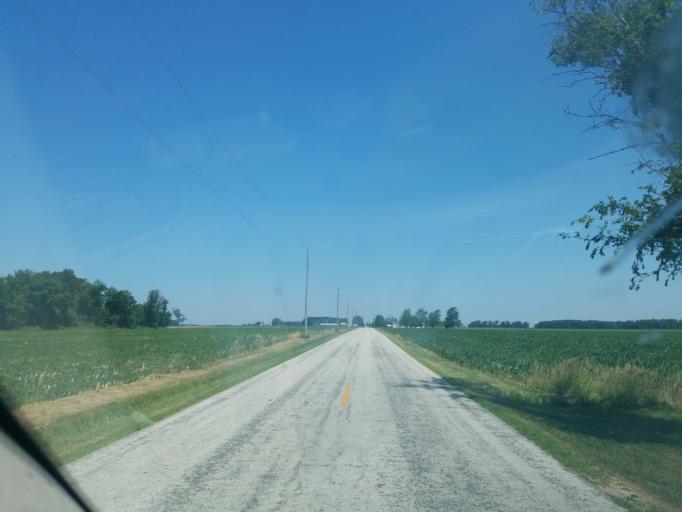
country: US
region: Ohio
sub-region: Mercer County
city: Rockford
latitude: 40.5859
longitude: -84.7084
